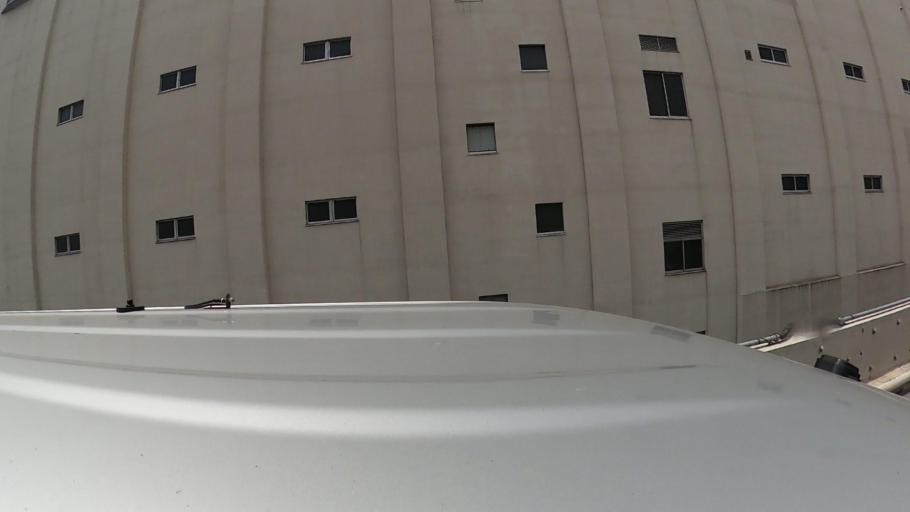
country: JP
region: Tokyo
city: Tokyo
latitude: 35.6382
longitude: 139.7525
